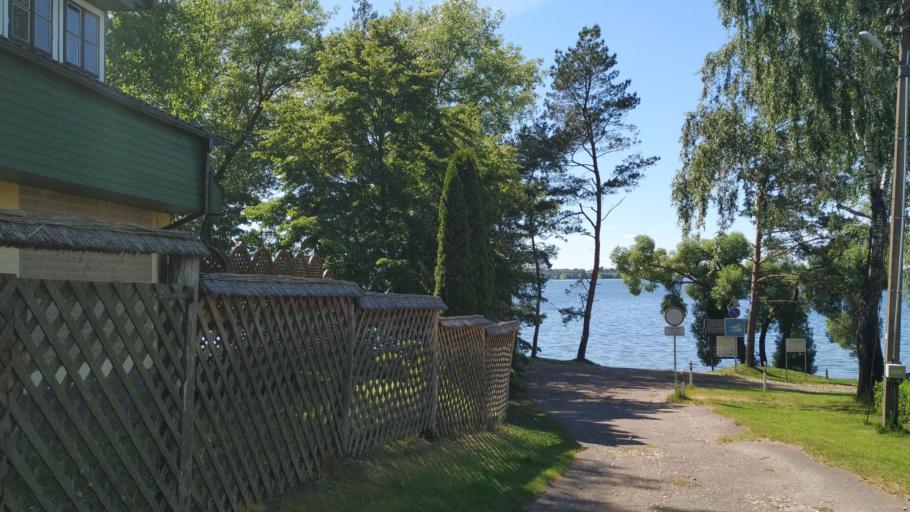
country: LT
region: Utenos apskritis
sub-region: Anyksciai
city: Anyksciai
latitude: 55.2939
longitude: 25.1161
